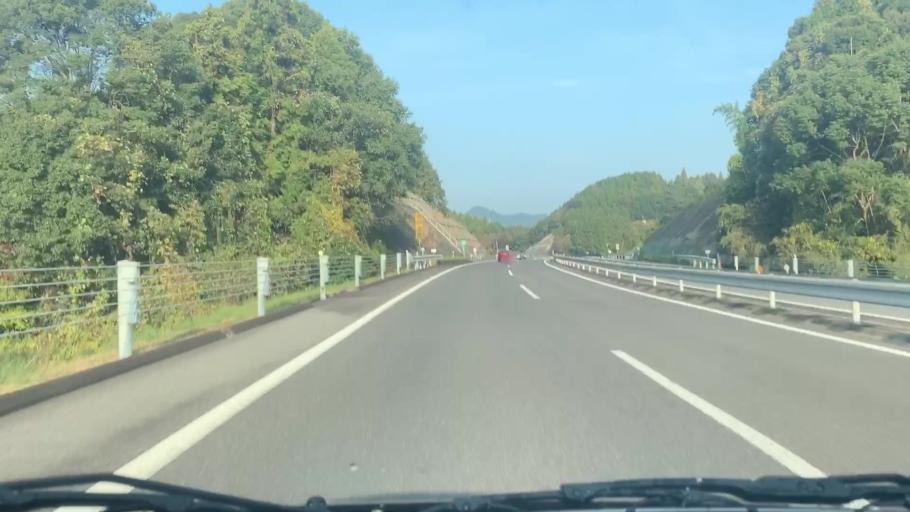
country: JP
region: Saga Prefecture
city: Ureshinomachi-shimojuku
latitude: 33.1505
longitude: 129.9360
